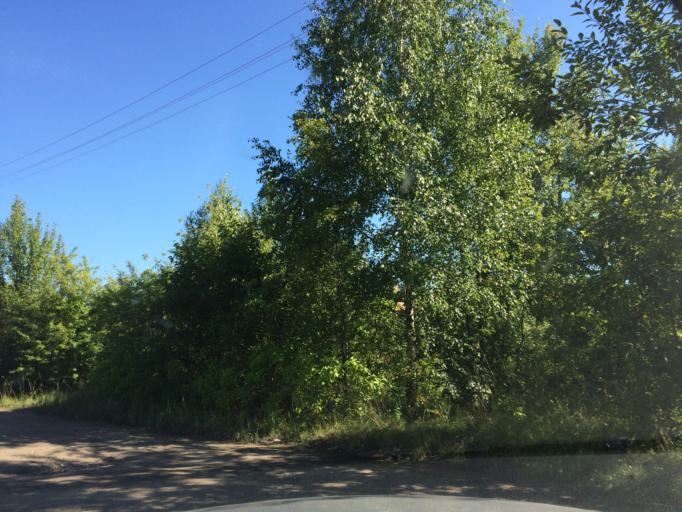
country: LV
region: Rezekne
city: Rezekne
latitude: 56.5277
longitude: 27.3378
